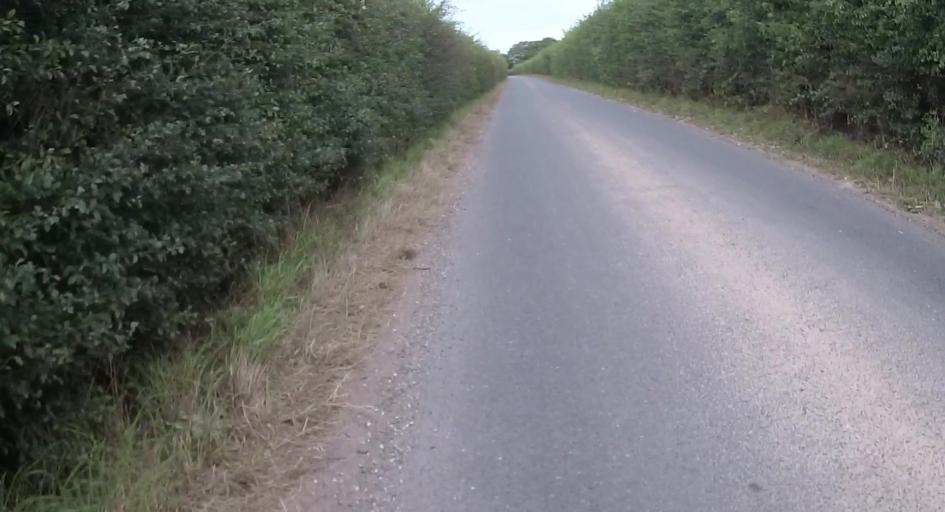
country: GB
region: England
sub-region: Hampshire
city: Overton
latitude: 51.1750
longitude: -1.2919
